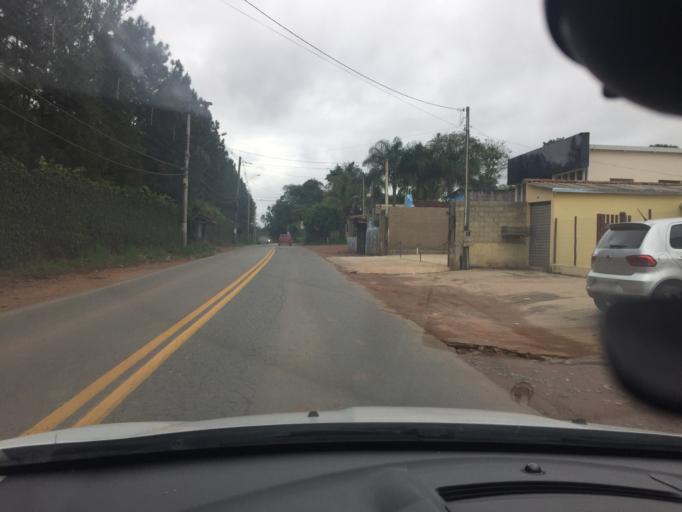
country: BR
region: Sao Paulo
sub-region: Jarinu
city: Jarinu
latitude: -23.1293
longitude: -46.7148
